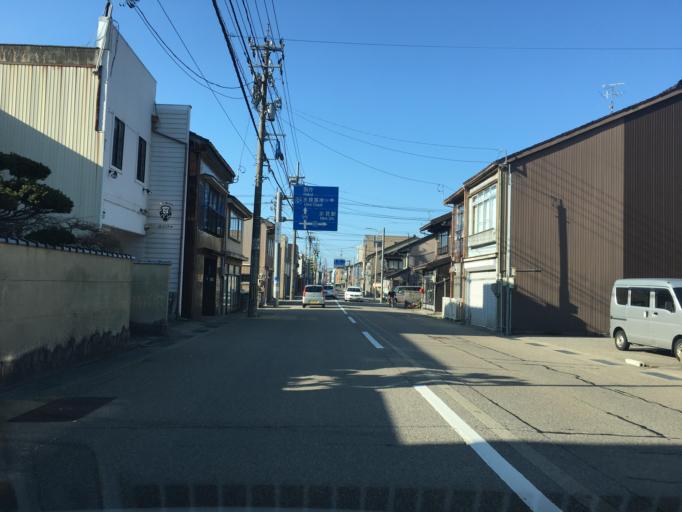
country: JP
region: Toyama
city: Himi
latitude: 36.8480
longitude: 136.9876
